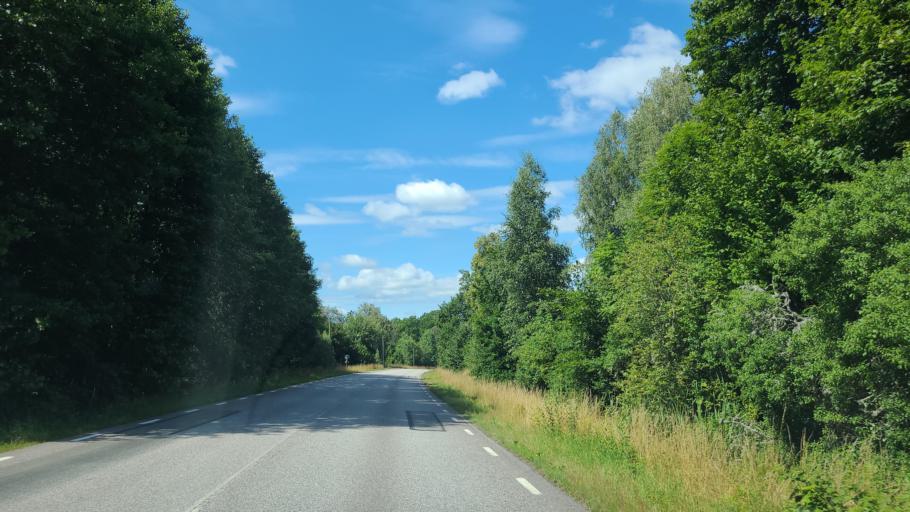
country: SE
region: Kalmar
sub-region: Emmaboda Kommun
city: Emmaboda
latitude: 56.5334
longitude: 15.6251
